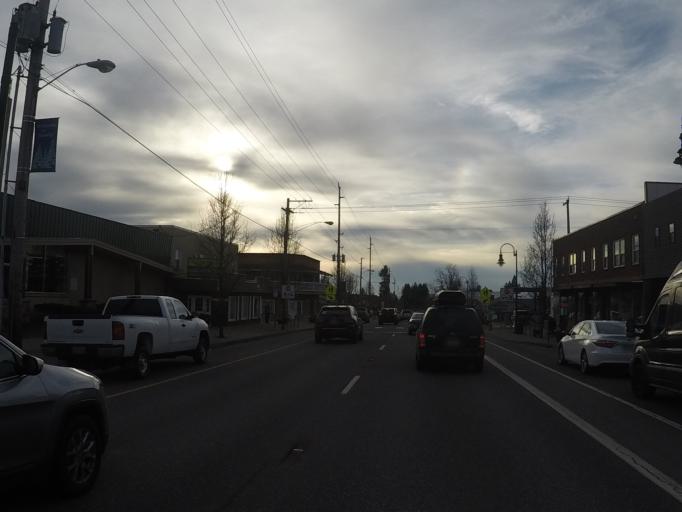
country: US
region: Oregon
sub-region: Clackamas County
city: Sandy
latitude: 45.3973
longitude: -122.2623
